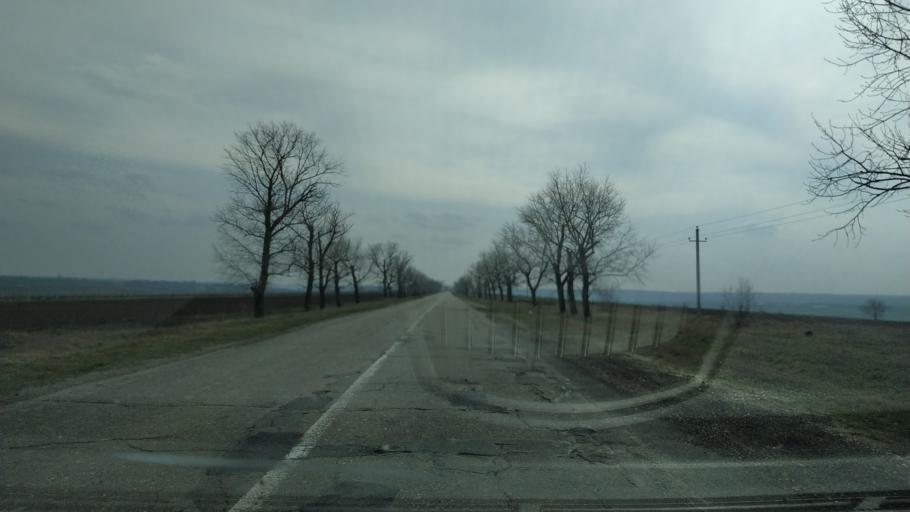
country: MD
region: Gagauzia
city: Vulcanesti
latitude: 45.7141
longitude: 28.3999
